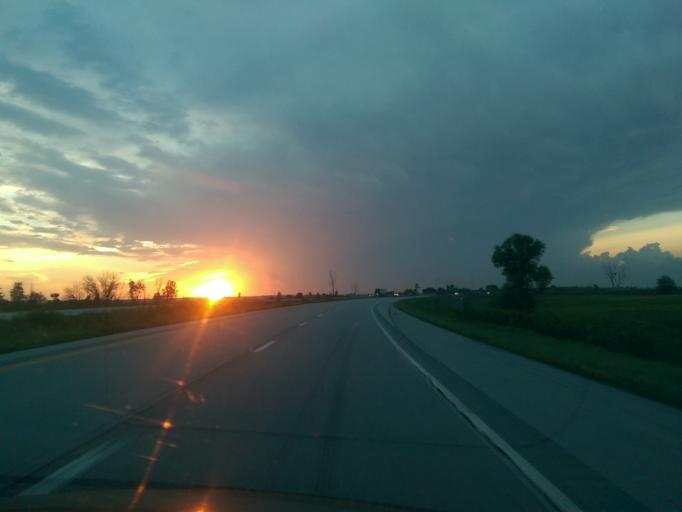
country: US
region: Iowa
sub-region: Fremont County
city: Hamburg
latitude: 40.5932
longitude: -95.6695
